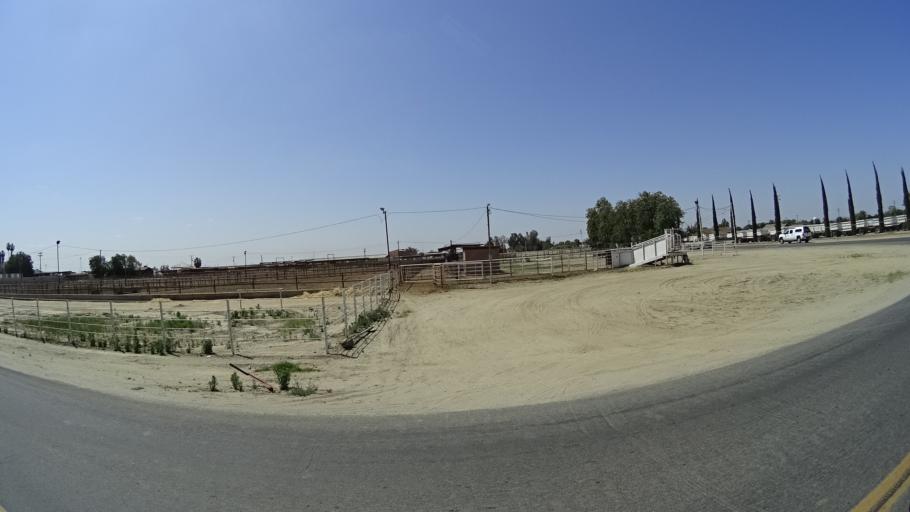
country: US
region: California
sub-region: Kings County
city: Home Garden
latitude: 36.3232
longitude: -119.6185
